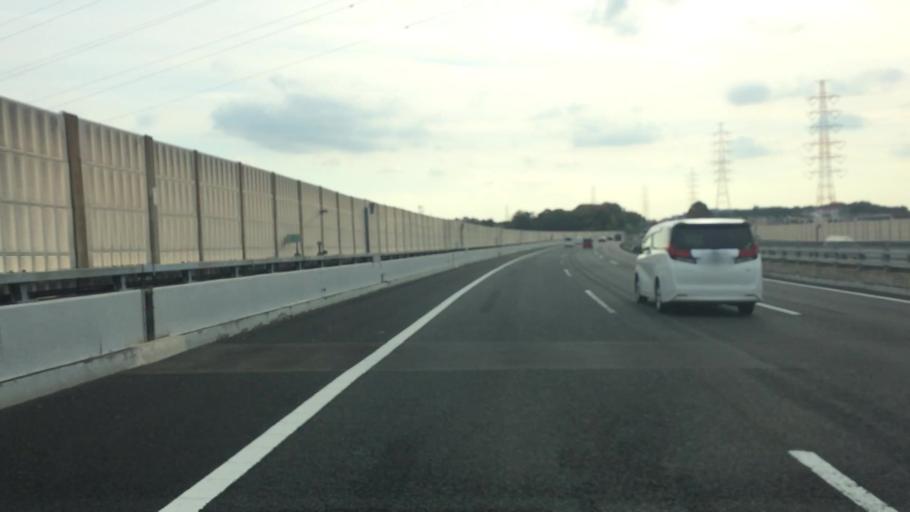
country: JP
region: Kanagawa
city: Yokohama
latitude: 35.5552
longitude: 139.6083
